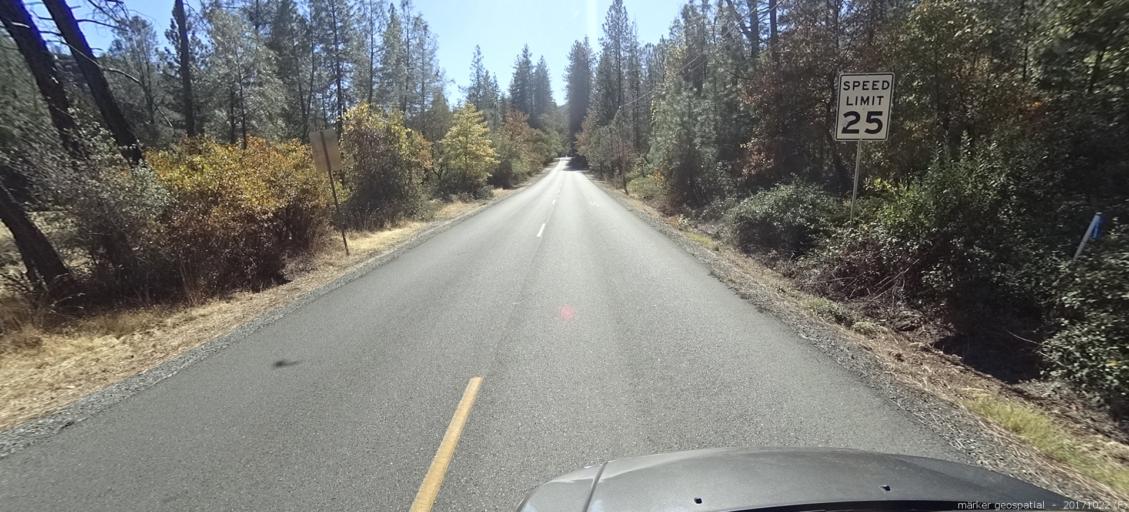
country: US
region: California
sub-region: Shasta County
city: Central Valley (historical)
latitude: 40.8770
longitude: -122.3889
